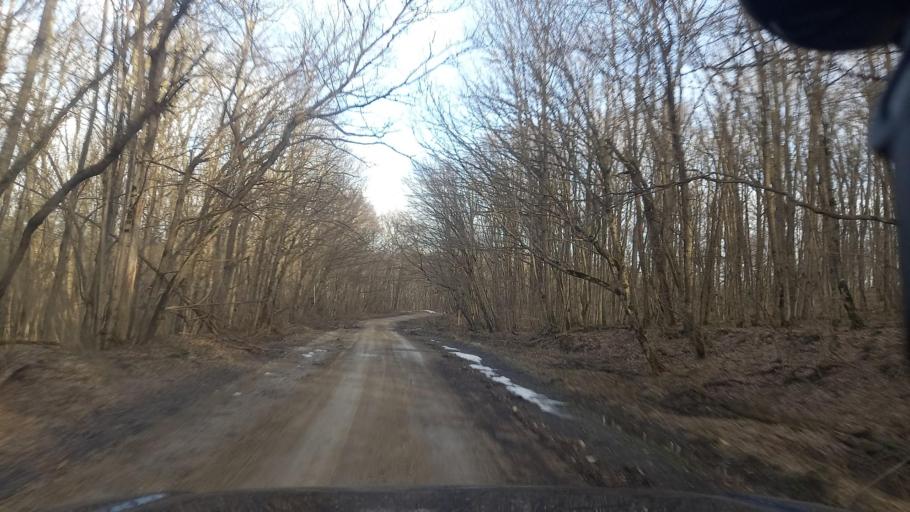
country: RU
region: Krasnodarskiy
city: Novodmitriyevskaya
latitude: 44.6998
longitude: 38.9712
